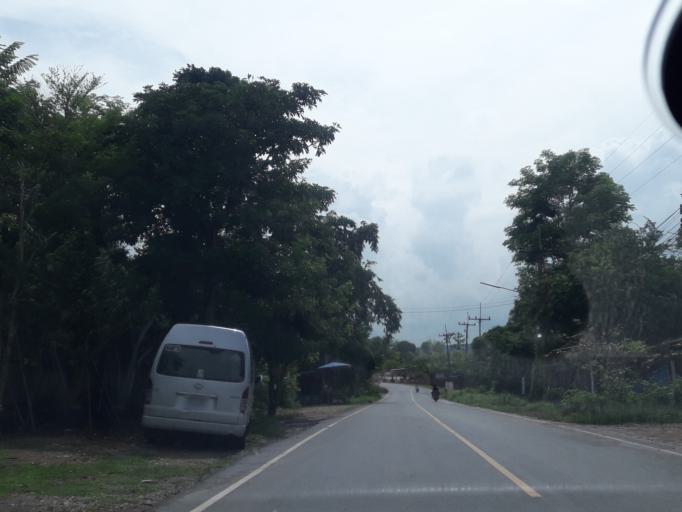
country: TH
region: Sara Buri
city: Wihan Daeng
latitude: 14.4213
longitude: 101.1302
